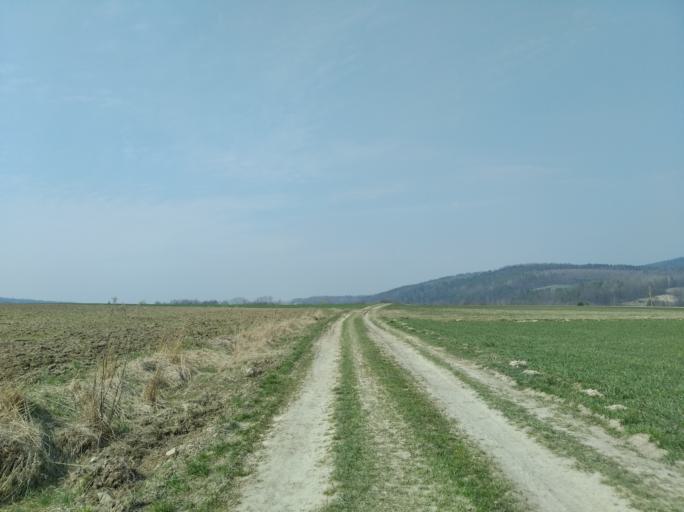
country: PL
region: Subcarpathian Voivodeship
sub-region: Powiat krosnienski
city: Korczyna
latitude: 49.7942
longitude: 21.8176
